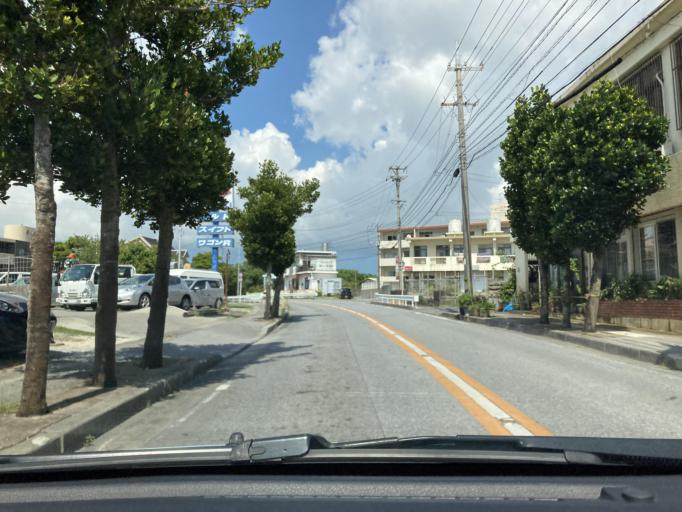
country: JP
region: Okinawa
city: Tomigusuku
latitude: 26.1606
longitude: 127.7448
